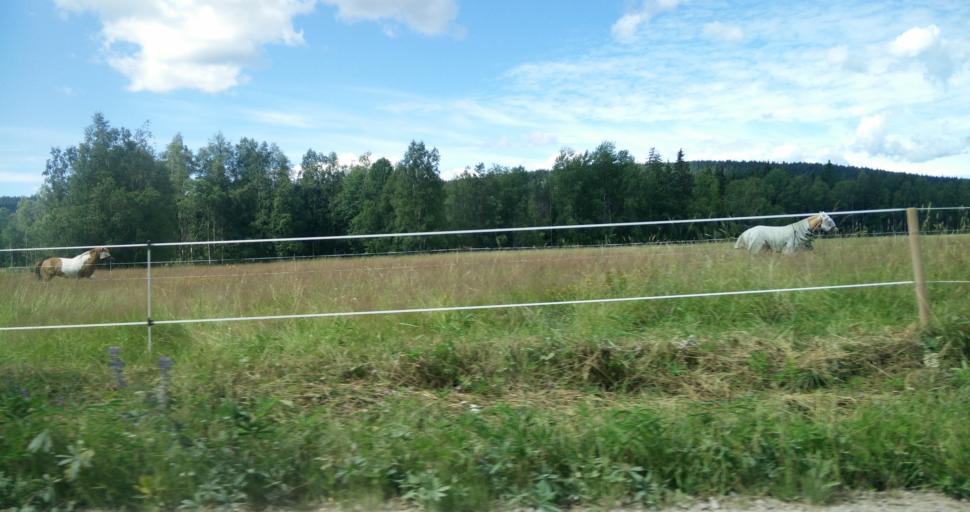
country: SE
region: Vaermland
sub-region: Hagfors Kommun
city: Ekshaerad
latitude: 60.0454
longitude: 13.4929
